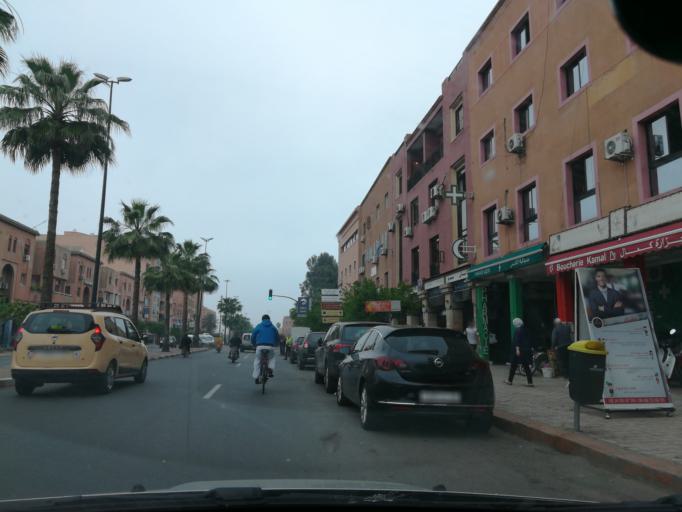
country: MA
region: Marrakech-Tensift-Al Haouz
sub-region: Marrakech
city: Marrakesh
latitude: 31.6471
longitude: -8.0006
